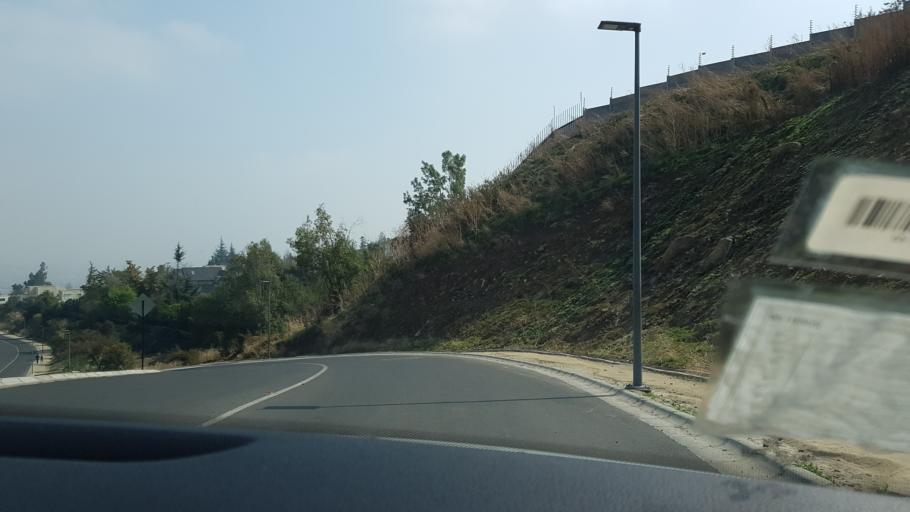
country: CL
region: Santiago Metropolitan
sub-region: Provincia de Santiago
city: Villa Presidente Frei, Nunoa, Santiago, Chile
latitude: -33.4809
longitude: -70.5188
